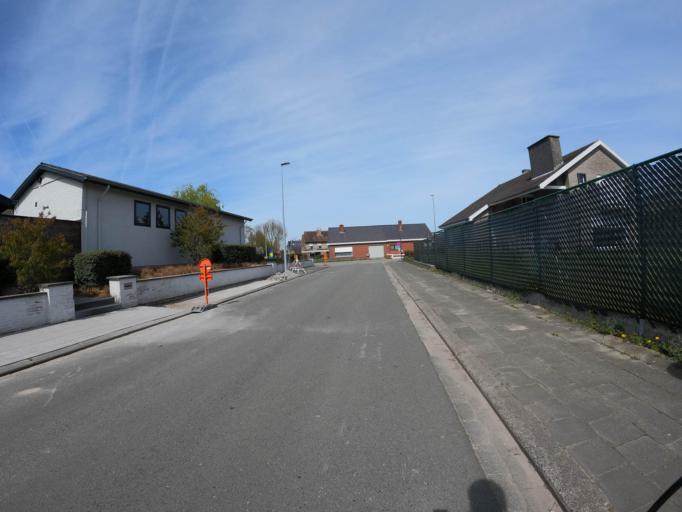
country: BE
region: Flanders
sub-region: Provincie West-Vlaanderen
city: Ruiselede
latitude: 51.0389
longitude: 3.3910
